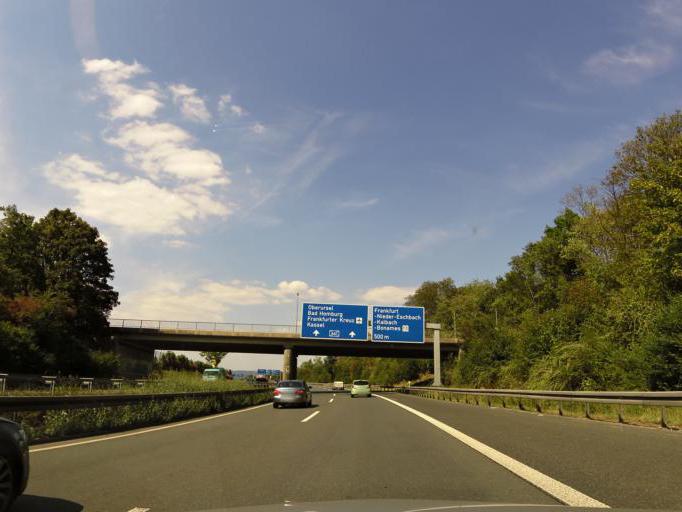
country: DE
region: Hesse
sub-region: Regierungsbezirk Darmstadt
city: Bad Homburg vor der Hoehe
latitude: 50.1880
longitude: 8.6580
